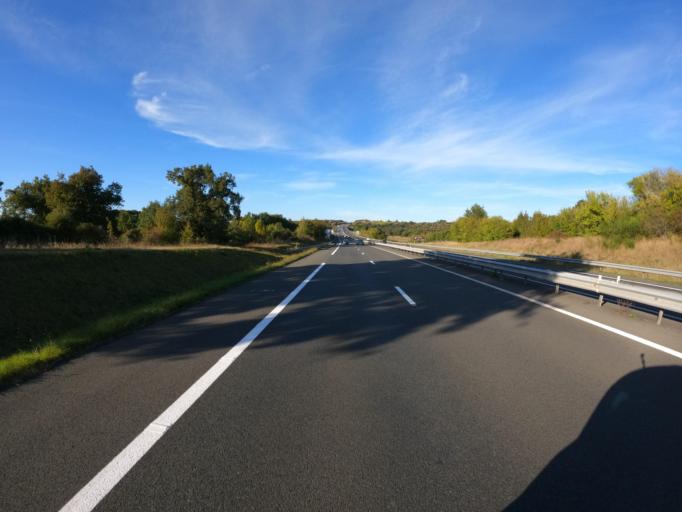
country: FR
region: Pays de la Loire
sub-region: Departement de Maine-et-Loire
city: Beaulieu-sur-Layon
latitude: 47.3044
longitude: -0.6078
